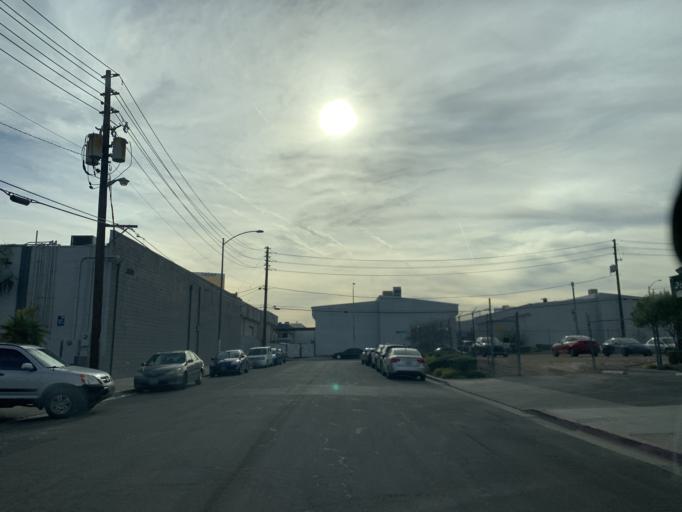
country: US
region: Nevada
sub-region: Clark County
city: Las Vegas
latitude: 36.1413
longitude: -115.1692
